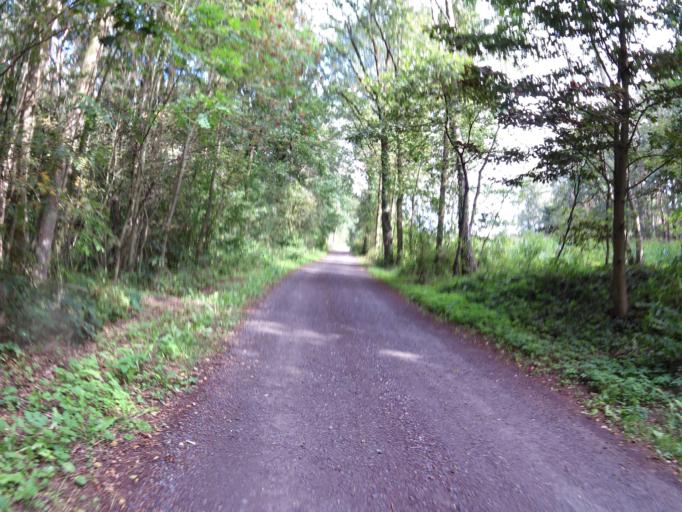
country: DE
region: Lower Saxony
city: Heeslingen
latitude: 53.2956
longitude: 9.3796
